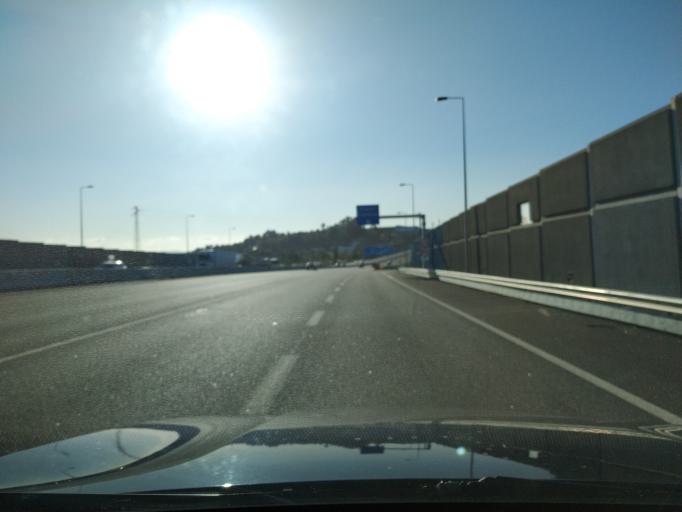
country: PT
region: Porto
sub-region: Vila Nova de Gaia
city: Vilar de Andorinho
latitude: 41.0963
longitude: -8.5918
